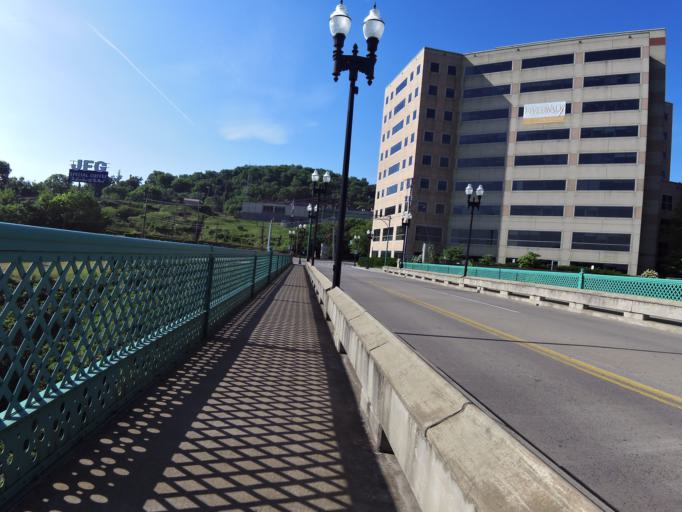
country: US
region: Tennessee
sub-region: Knox County
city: Knoxville
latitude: 35.9572
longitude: -83.9139
